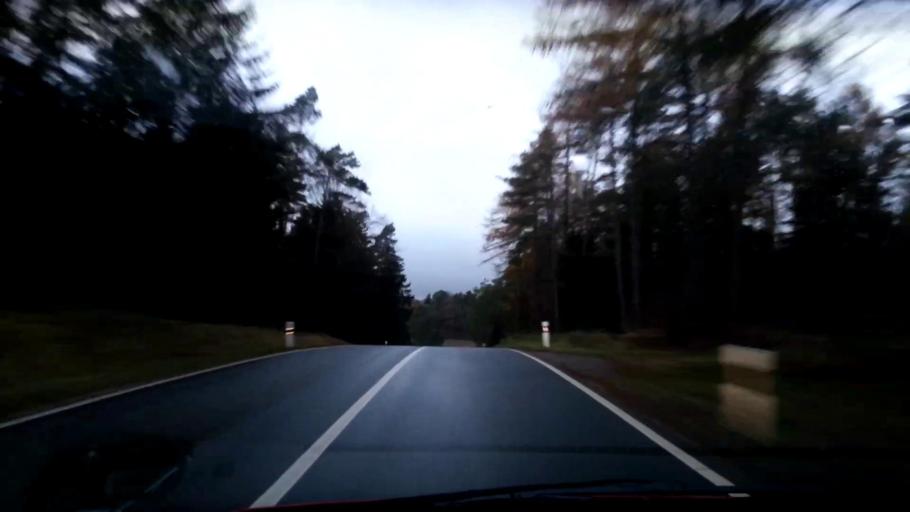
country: DE
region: Bavaria
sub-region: Upper Franconia
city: Konigsfeld
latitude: 49.9431
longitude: 11.1850
